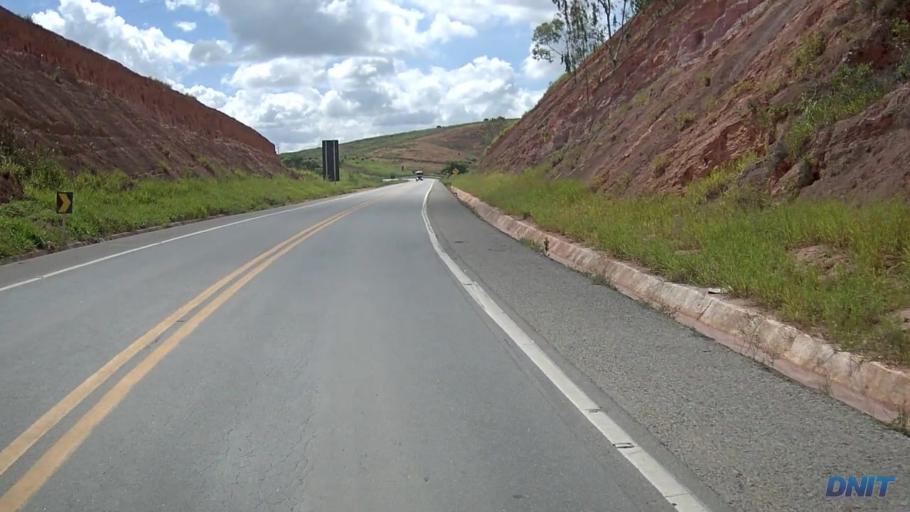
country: BR
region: Minas Gerais
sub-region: Governador Valadares
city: Governador Valadares
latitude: -19.0662
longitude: -42.1695
